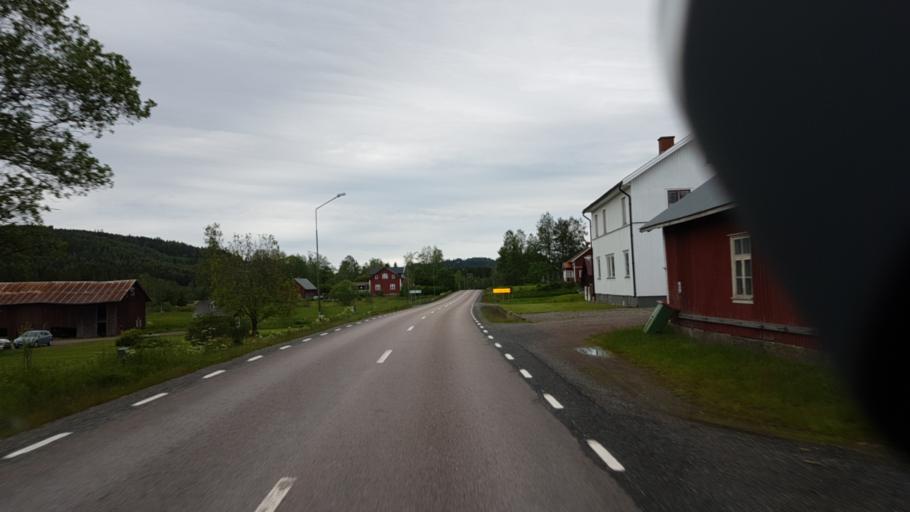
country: SE
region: Vaermland
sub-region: Arjangs Kommun
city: Arjaeng
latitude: 59.5870
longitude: 12.1283
